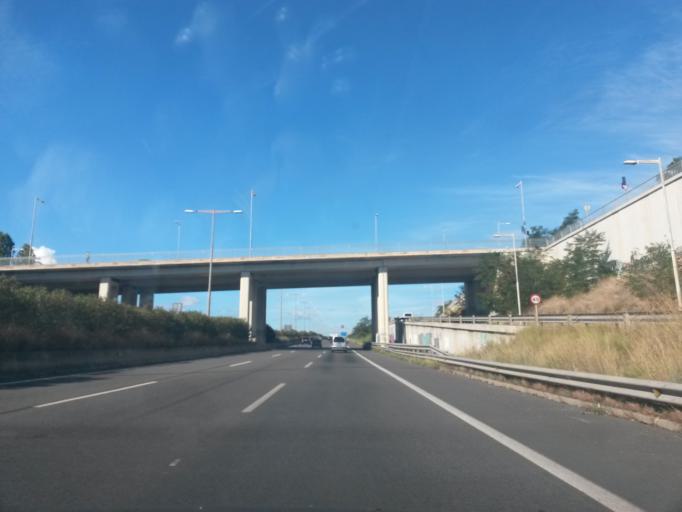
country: ES
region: Catalonia
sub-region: Provincia de Barcelona
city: Badalona
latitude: 41.4651
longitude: 2.2393
